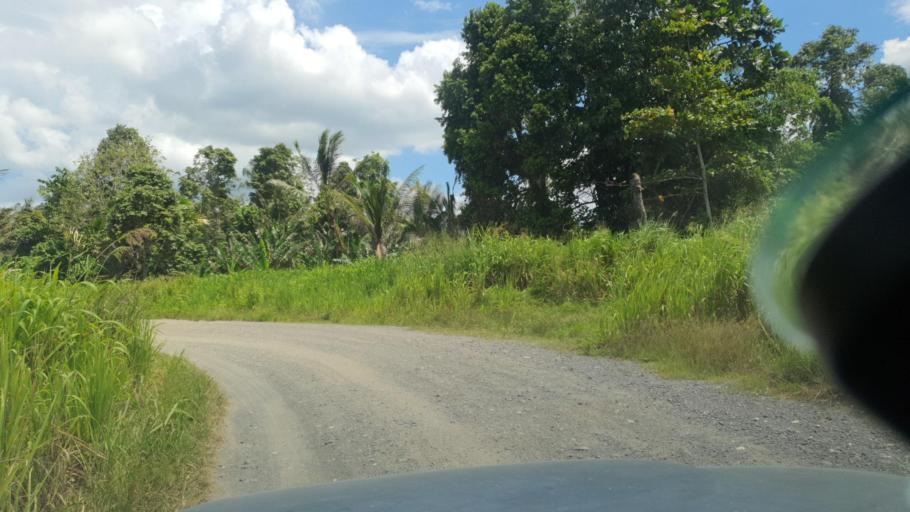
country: SB
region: Guadalcanal
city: Honiara
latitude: -9.4449
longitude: 160.1523
